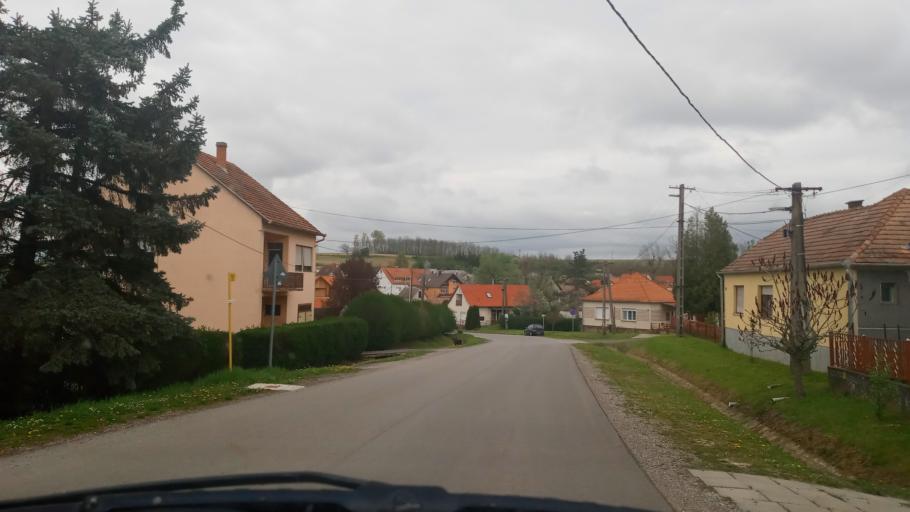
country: HU
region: Baranya
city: Kozarmisleny
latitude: 46.0397
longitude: 18.3484
